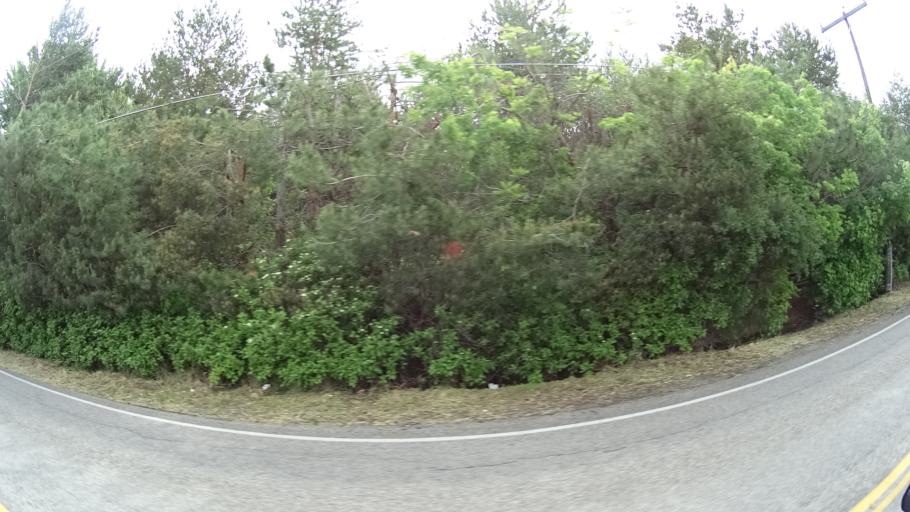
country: US
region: Idaho
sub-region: Ada County
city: Eagle
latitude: 43.7118
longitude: -116.3540
